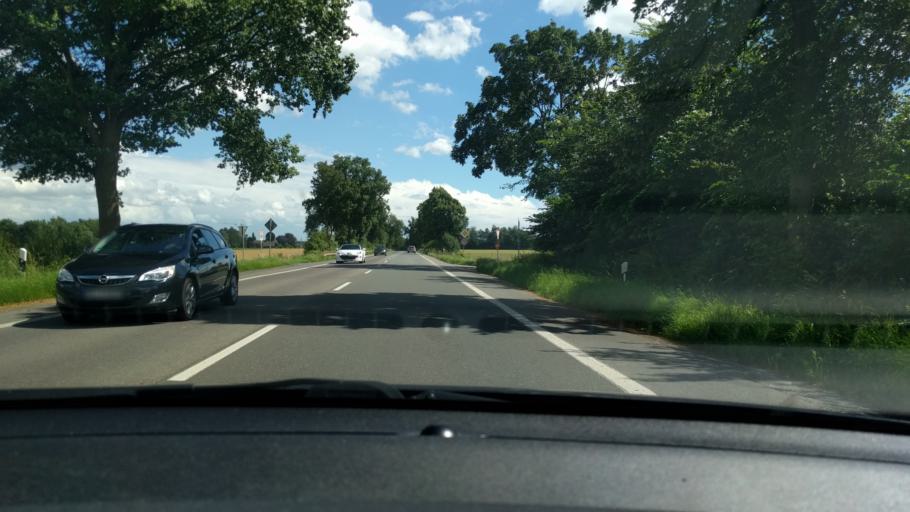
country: DE
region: North Rhine-Westphalia
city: Datteln
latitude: 51.6646
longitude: 7.3313
